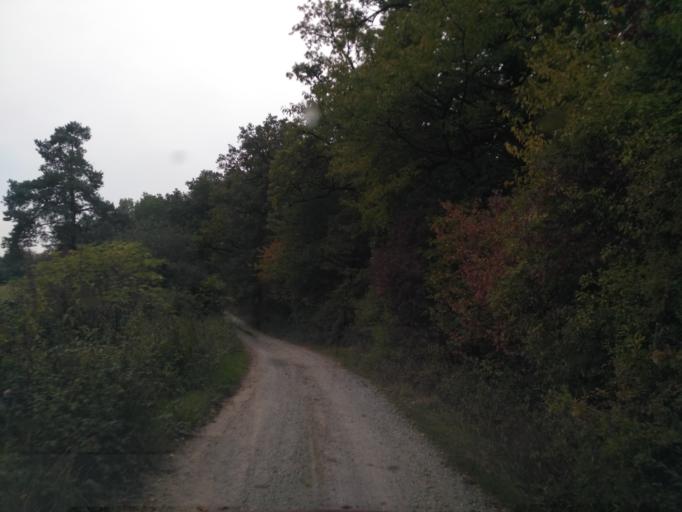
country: SK
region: Kosicky
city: Kosice
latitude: 48.7980
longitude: 21.2731
